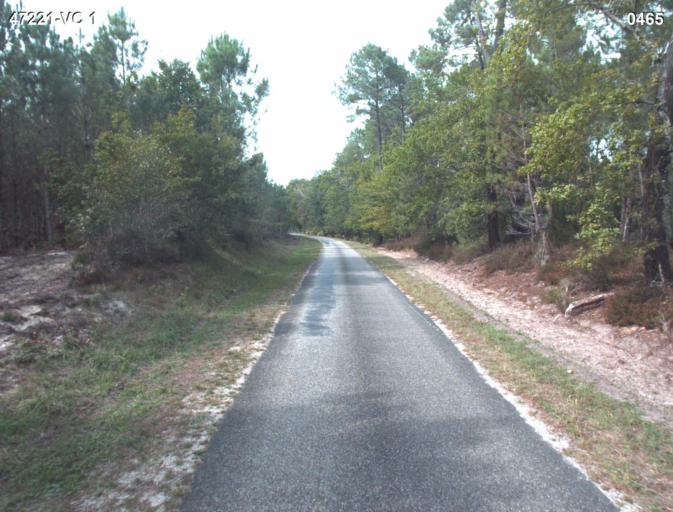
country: FR
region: Aquitaine
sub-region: Departement du Lot-et-Garonne
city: Mezin
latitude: 44.1136
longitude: 0.2234
